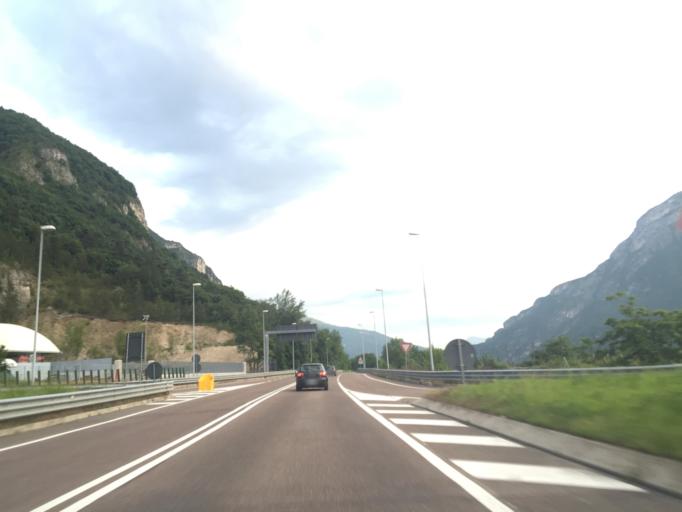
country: IT
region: Trentino-Alto Adige
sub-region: Provincia di Trento
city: Aldeno
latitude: 45.9791
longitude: 11.1149
